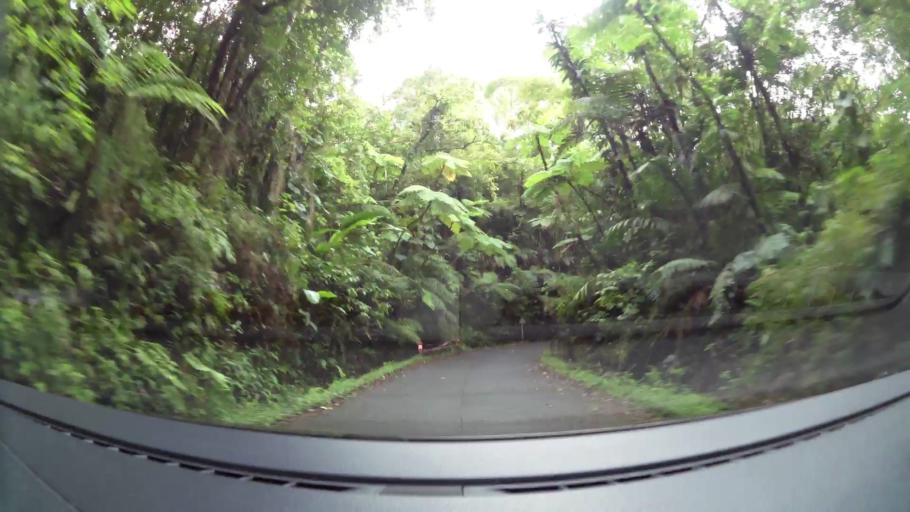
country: GP
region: Guadeloupe
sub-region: Guadeloupe
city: Trois-Rivieres
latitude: 16.0353
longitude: -61.6301
